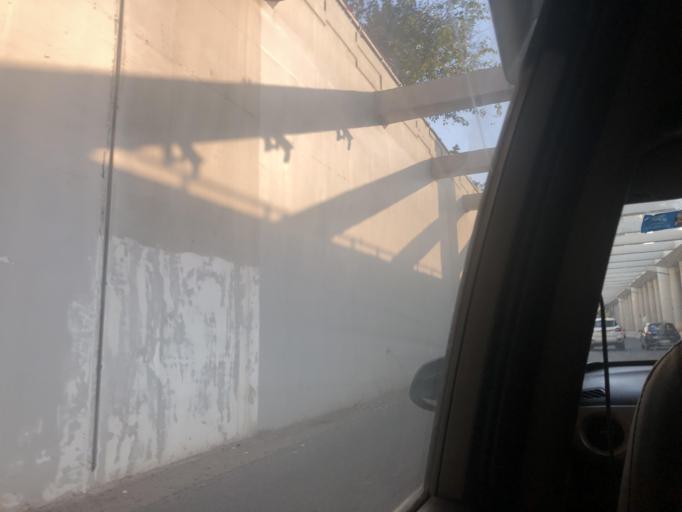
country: IN
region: Haryana
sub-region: Gurgaon
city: Gurgaon
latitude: 28.4844
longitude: 77.0951
